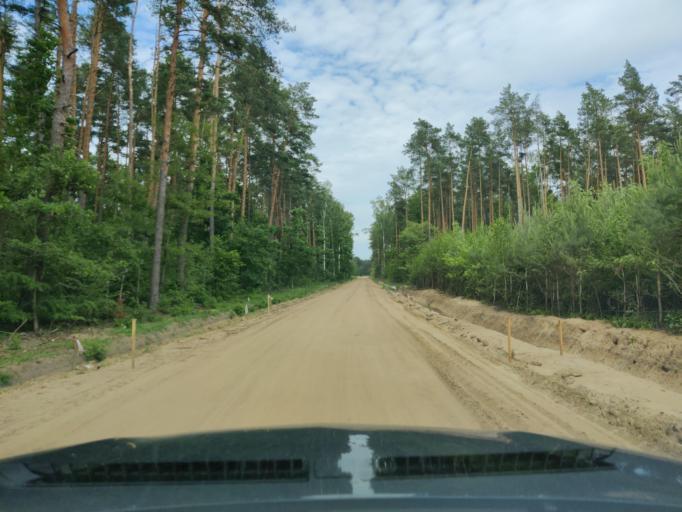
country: PL
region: Masovian Voivodeship
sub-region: Powiat pultuski
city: Pultusk
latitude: 52.7212
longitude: 21.1498
